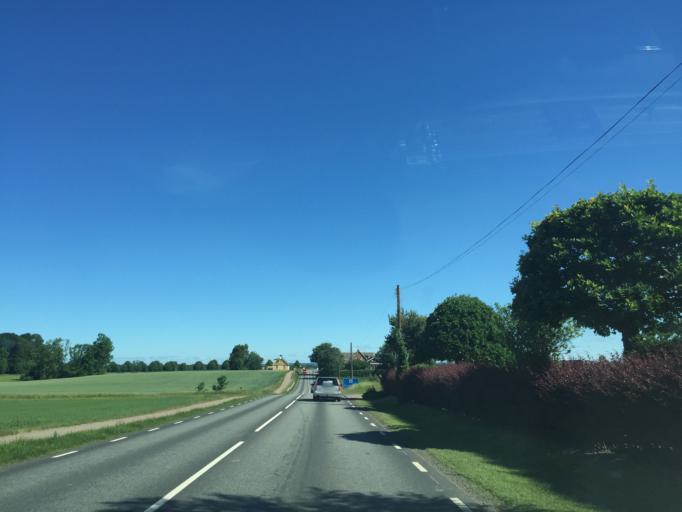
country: SE
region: Skane
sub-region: Angelholms Kommun
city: AEngelholm
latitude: 56.2120
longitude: 12.8565
